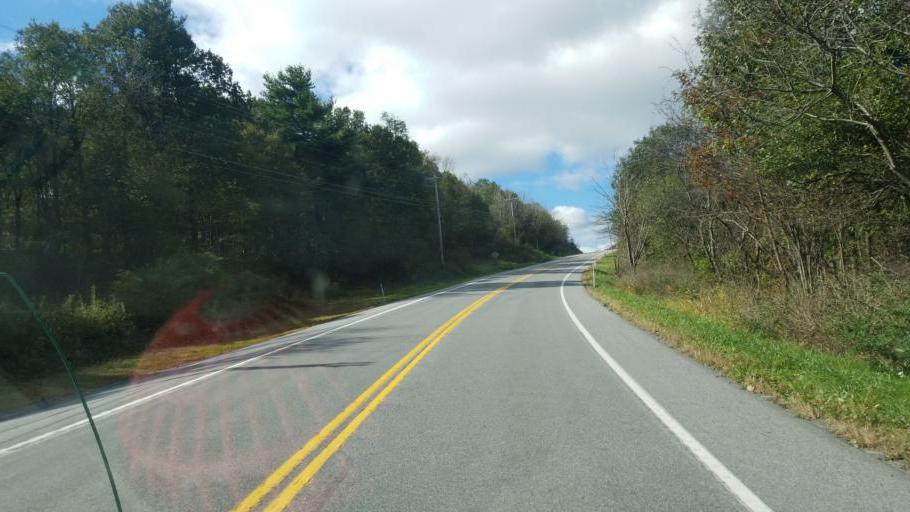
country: US
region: Pennsylvania
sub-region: Bedford County
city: Earlston
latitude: 40.0152
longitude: -78.1961
